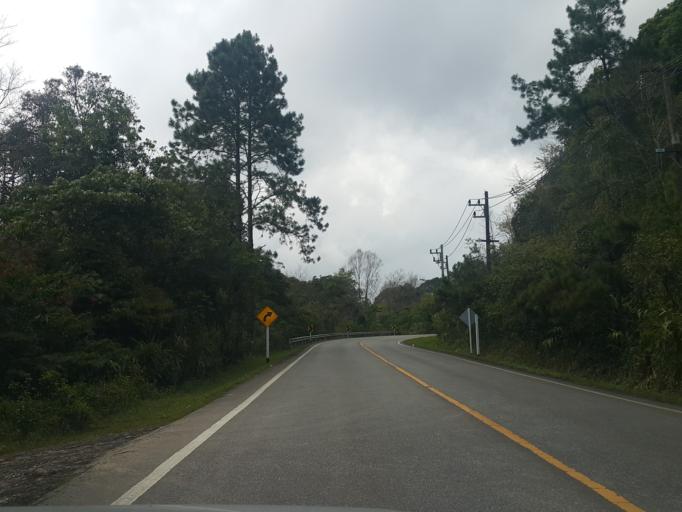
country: TH
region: Chiang Mai
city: Mae Chaem
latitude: 18.5081
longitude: 98.5108
